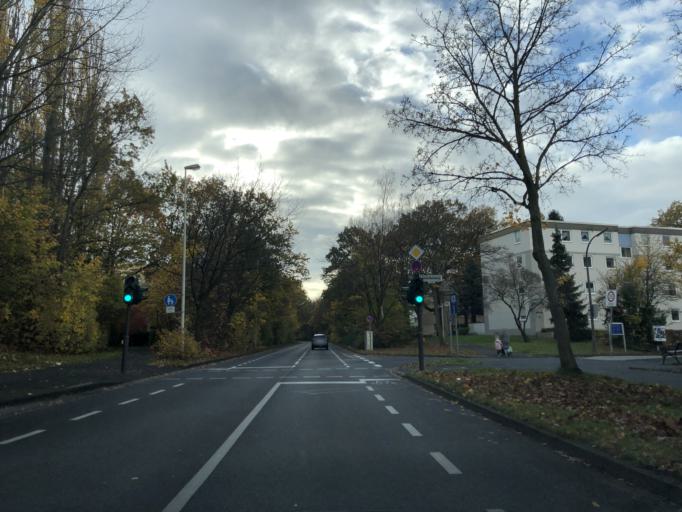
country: DE
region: North Rhine-Westphalia
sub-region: Regierungsbezirk Koln
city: Konigswinter
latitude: 50.6628
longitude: 7.1553
